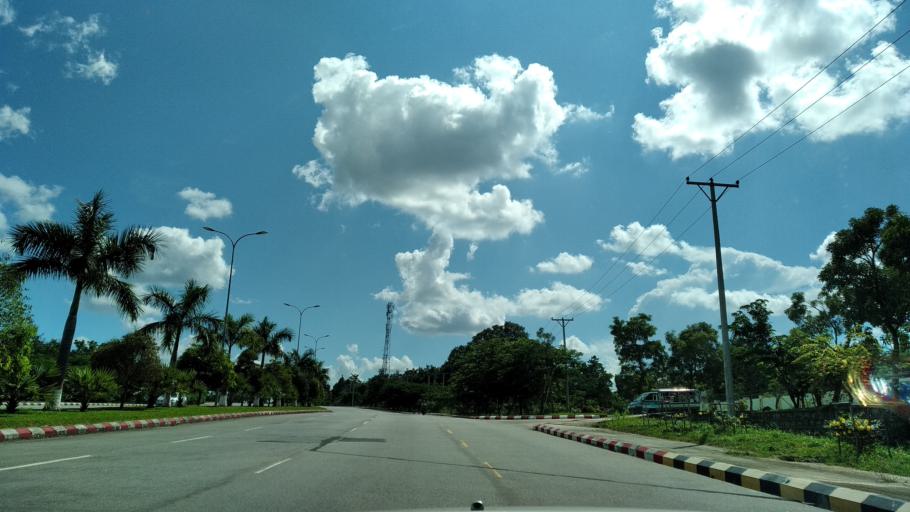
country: MM
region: Mandalay
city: Nay Pyi Taw
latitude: 19.7908
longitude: 96.1456
